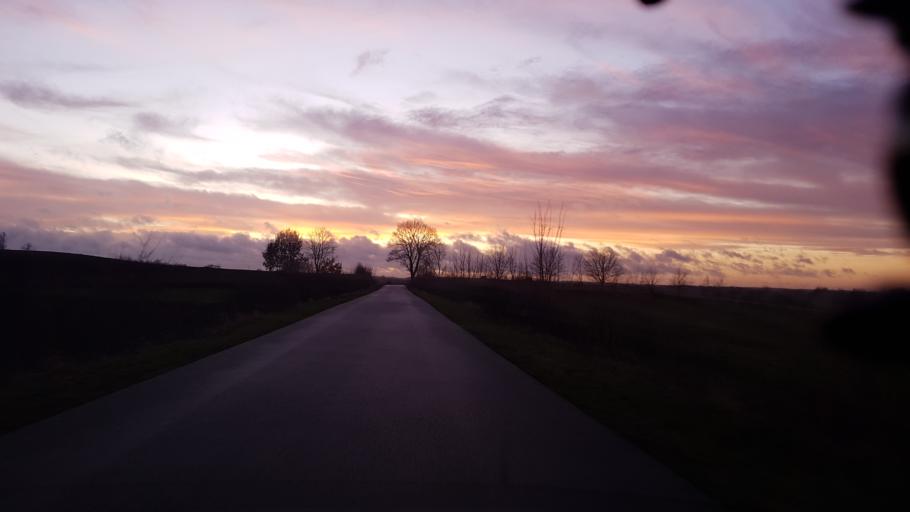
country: PL
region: Pomeranian Voivodeship
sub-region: Powiat bytowski
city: Tuchomie
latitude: 54.1298
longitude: 17.3536
